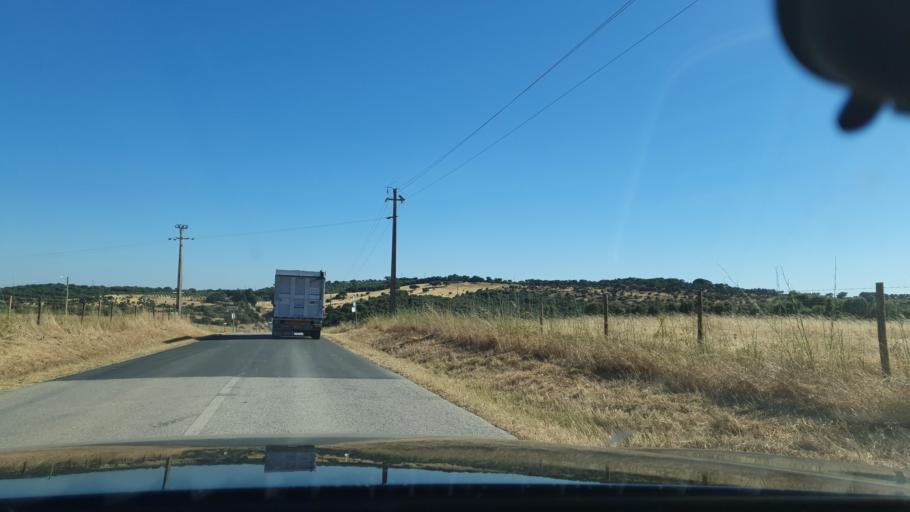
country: PT
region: Evora
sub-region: Alandroal
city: Alandroal
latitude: 38.7252
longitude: -7.4057
